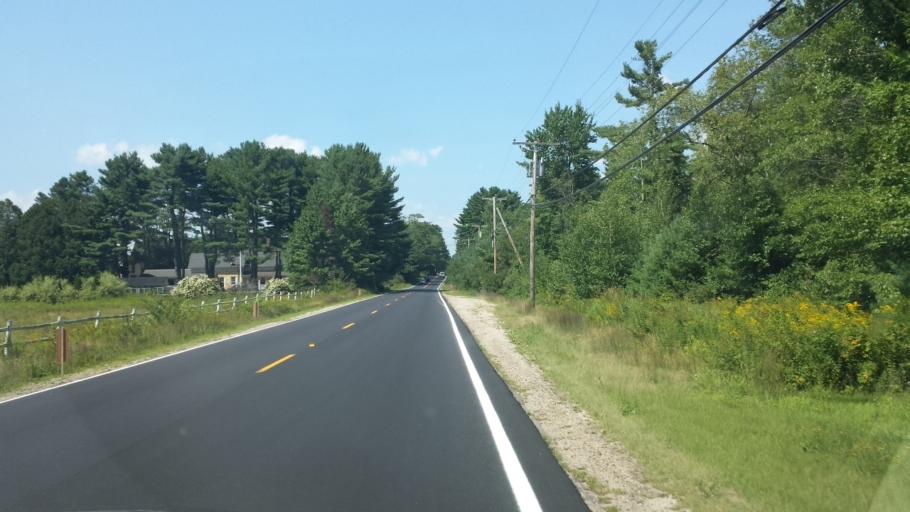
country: US
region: Maine
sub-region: York County
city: Arundel
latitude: 43.4003
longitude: -70.4863
